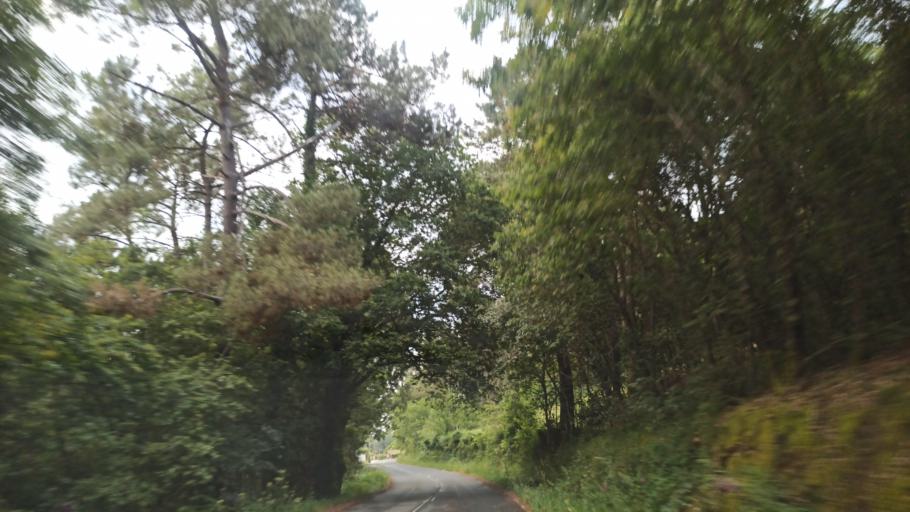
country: ES
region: Galicia
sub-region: Provincia da Coruna
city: Santiso
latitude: 42.8276
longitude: -8.1288
